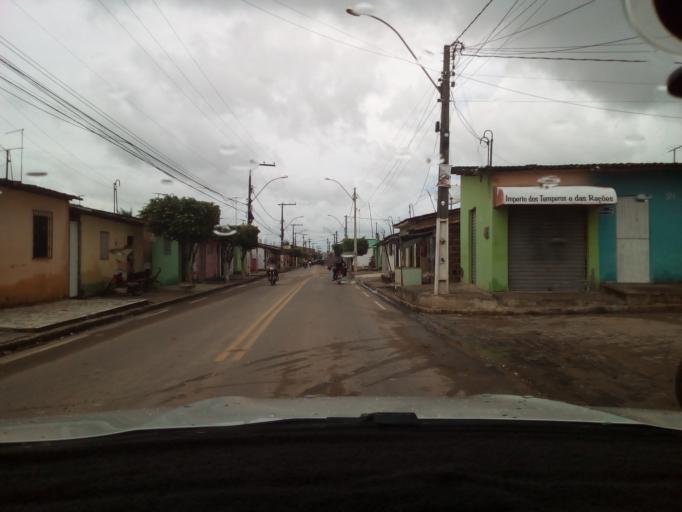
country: BR
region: Paraiba
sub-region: Pedras De Fogo
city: Pedras de Fogo
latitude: -7.4045
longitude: -35.1081
